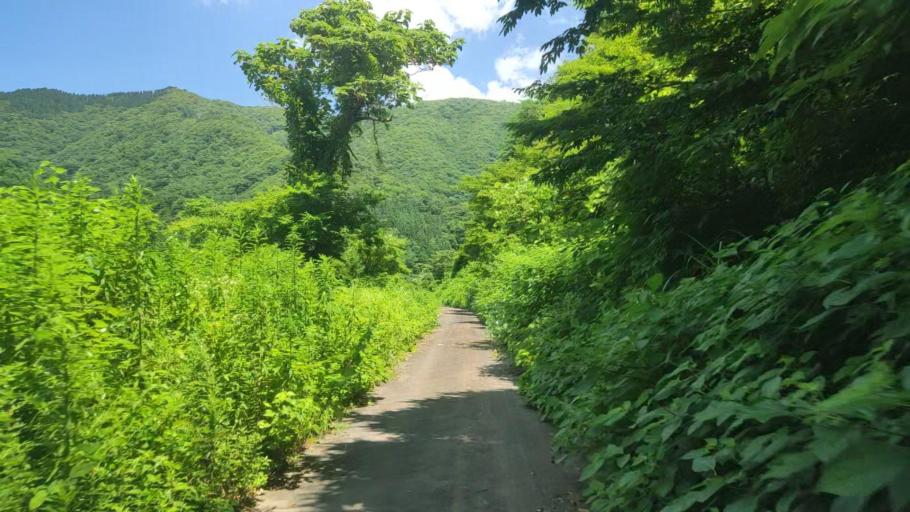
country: JP
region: Fukui
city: Ono
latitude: 35.8978
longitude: 136.5133
